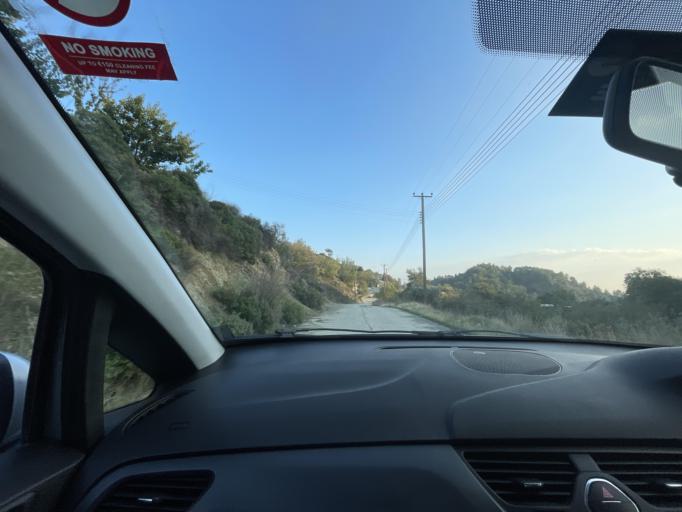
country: CY
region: Limassol
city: Pelendri
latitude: 34.8897
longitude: 32.9713
